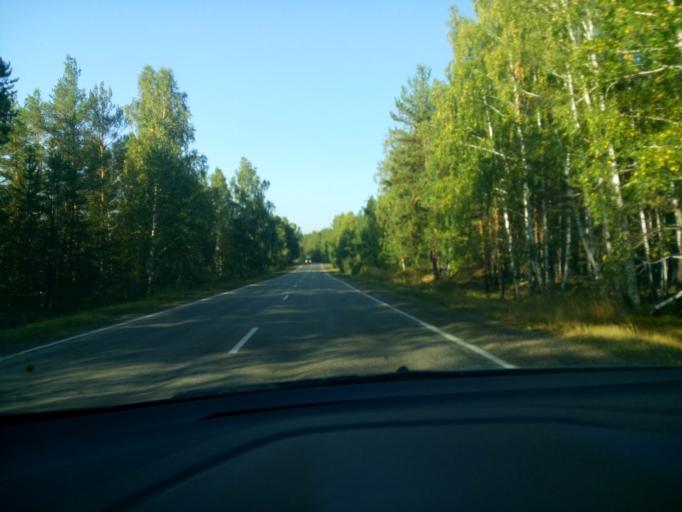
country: RU
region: Chelyabinsk
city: Kasli
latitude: 55.8650
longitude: 60.6900
